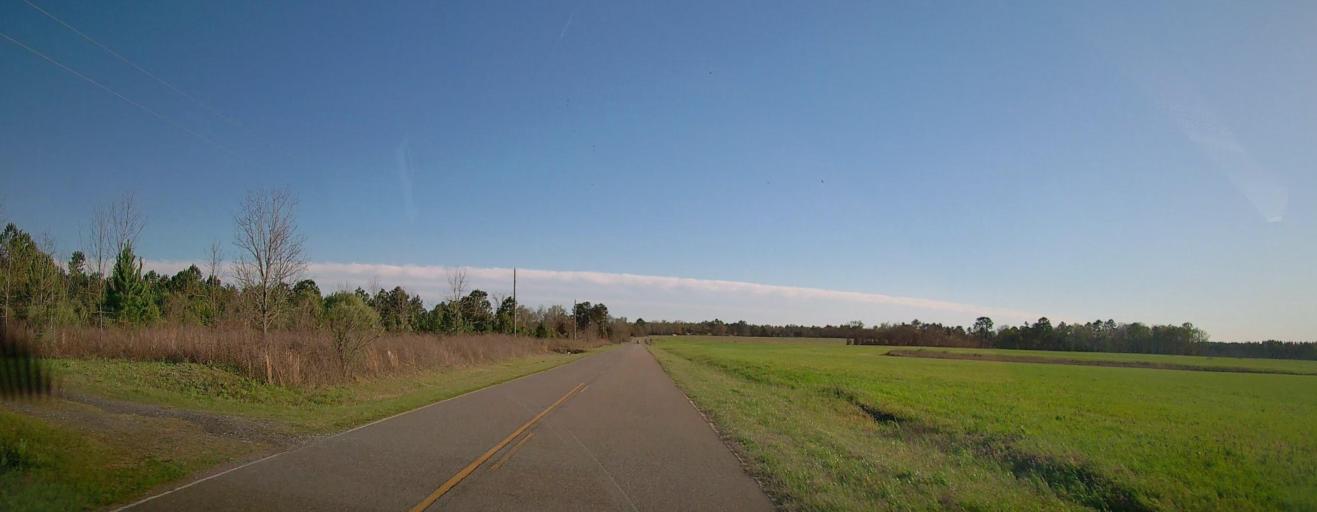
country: US
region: Georgia
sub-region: Pulaski County
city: Hawkinsville
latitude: 32.2510
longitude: -83.5878
